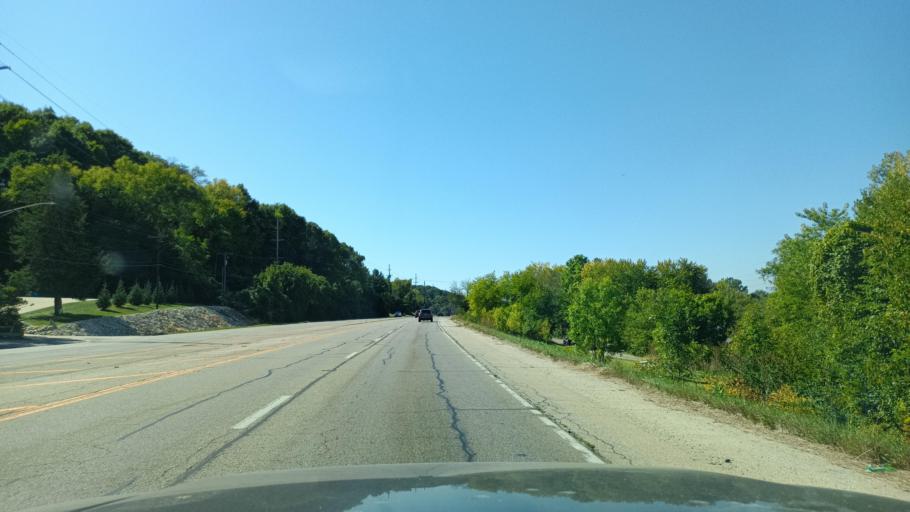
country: US
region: Illinois
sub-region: Tazewell County
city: East Peoria
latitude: 40.6815
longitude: -89.5555
